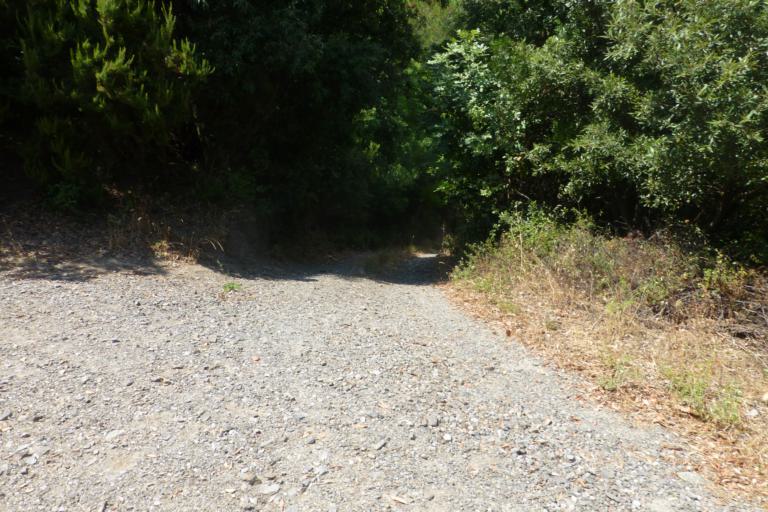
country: IT
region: Calabria
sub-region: Provincia di Reggio Calabria
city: Pazzano
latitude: 38.4776
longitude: 16.4363
